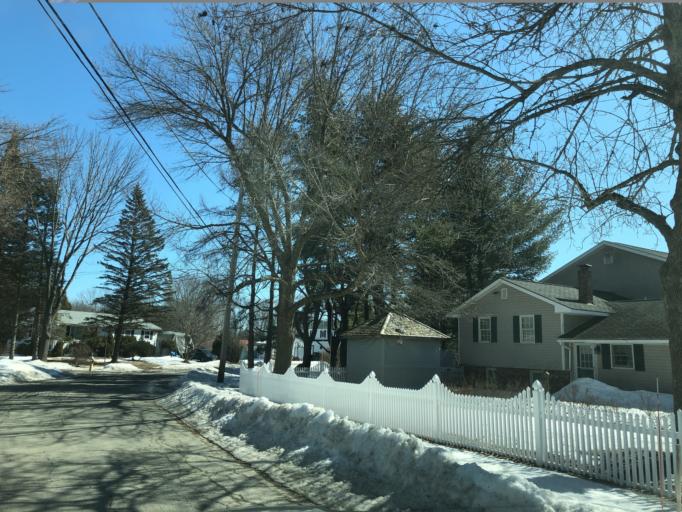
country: US
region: Maine
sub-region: Penobscot County
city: Brewer
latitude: 44.8205
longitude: -68.7557
